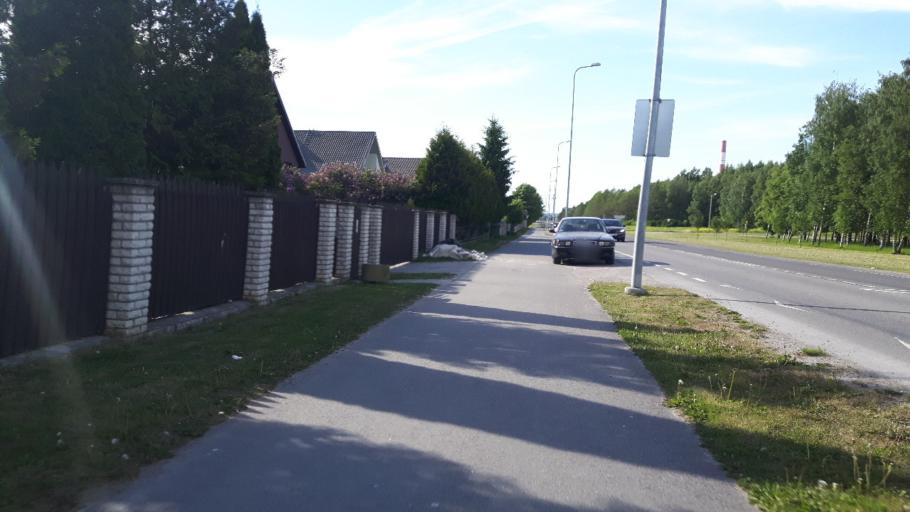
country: EE
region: Harju
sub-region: Joelaehtme vald
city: Loo
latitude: 59.4365
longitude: 24.9409
